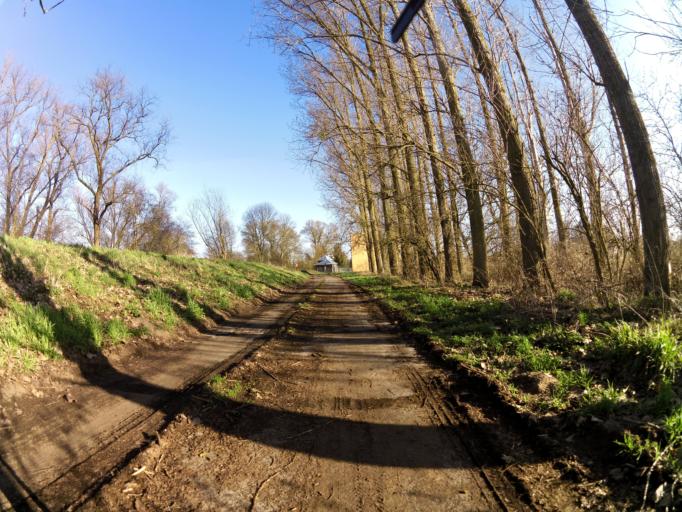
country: PL
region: West Pomeranian Voivodeship
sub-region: Powiat policki
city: Nowe Warpno
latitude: 53.6994
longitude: 14.3660
